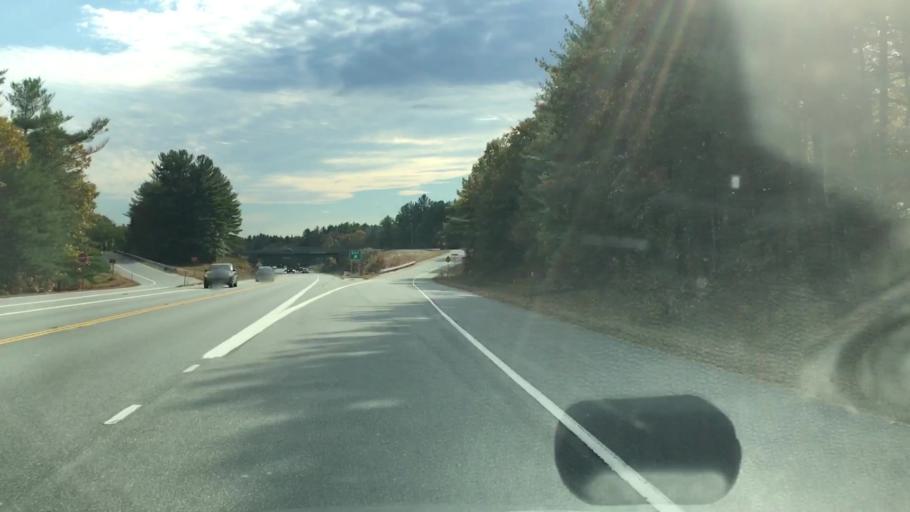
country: US
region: New Hampshire
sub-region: Hillsborough County
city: Milford
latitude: 42.8688
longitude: -71.6138
